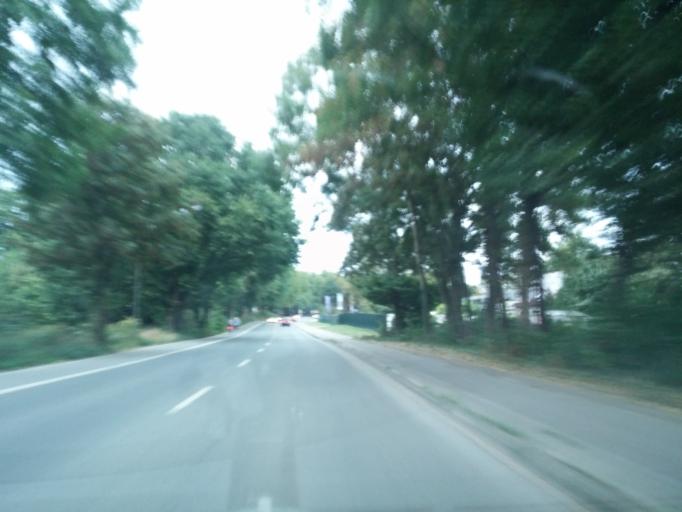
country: DE
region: North Rhine-Westphalia
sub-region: Regierungsbezirk Munster
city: Gladbeck
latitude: 51.5707
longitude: 7.0306
